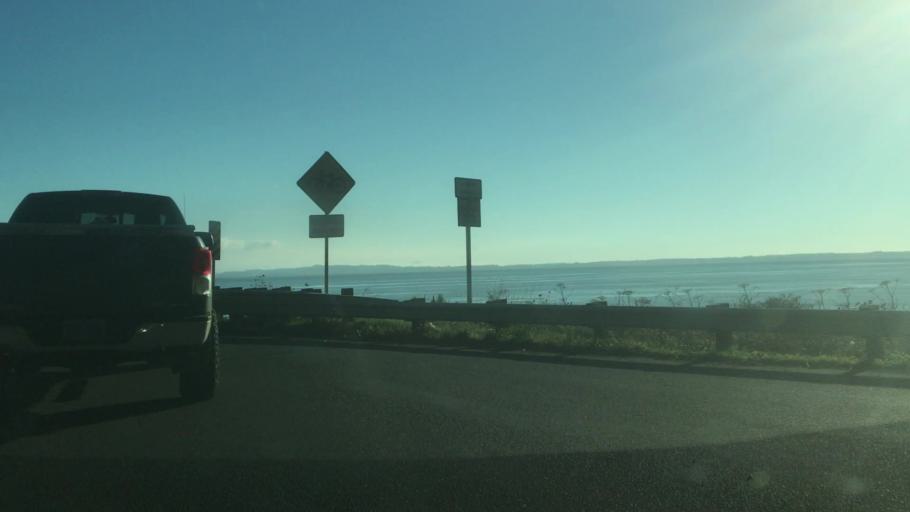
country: US
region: Oregon
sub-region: Clatsop County
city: Astoria
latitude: 46.2410
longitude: -123.8750
